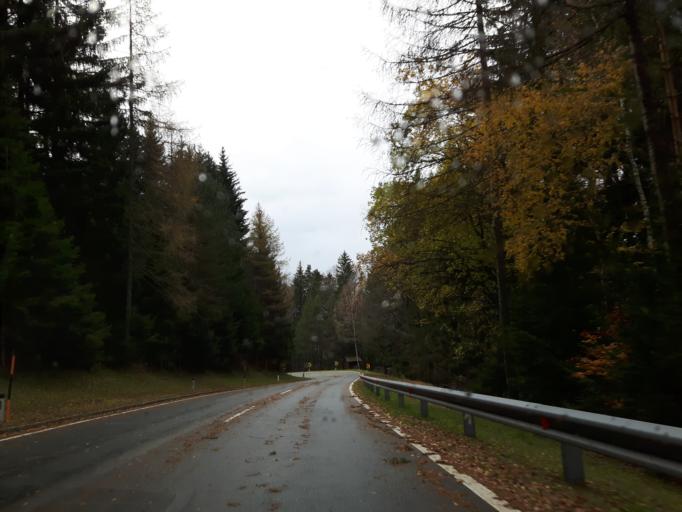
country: AT
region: Carinthia
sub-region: Politischer Bezirk Wolfsberg
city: Lavamund
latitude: 46.6488
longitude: 14.9859
